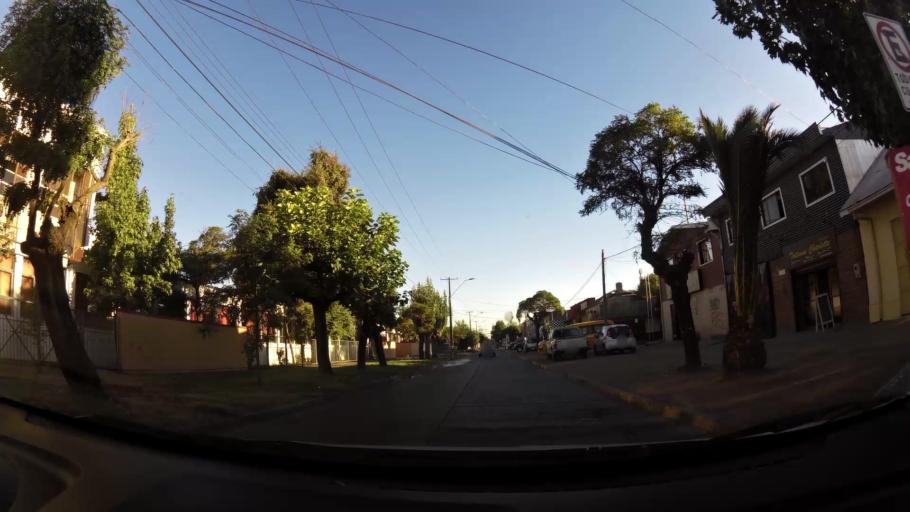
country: CL
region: Maule
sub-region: Provincia de Curico
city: Curico
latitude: -34.9772
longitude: -71.2412
